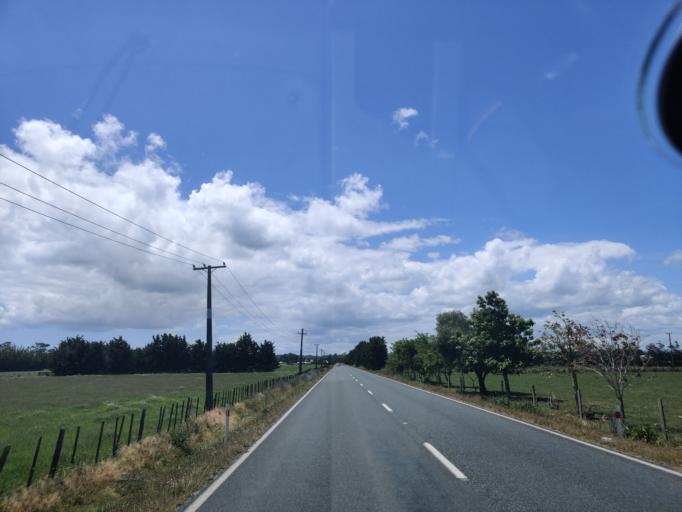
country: NZ
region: Northland
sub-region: Far North District
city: Kaitaia
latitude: -35.0254
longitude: 173.2400
